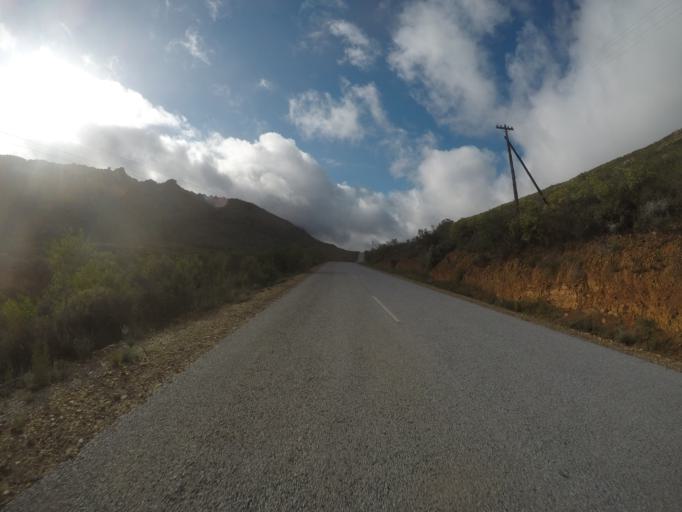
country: ZA
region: Western Cape
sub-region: West Coast District Municipality
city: Clanwilliam
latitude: -32.3673
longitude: 18.8618
